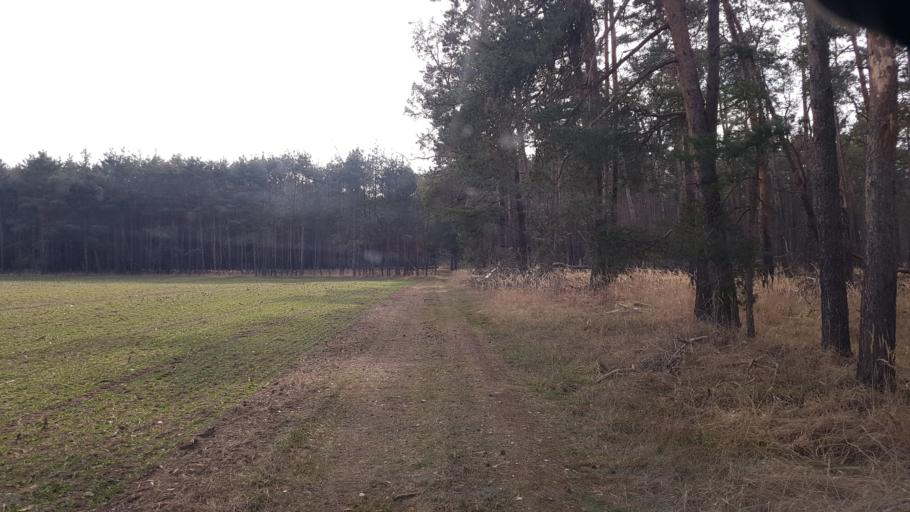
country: DE
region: Brandenburg
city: Schlieben
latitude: 51.6672
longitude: 13.3644
